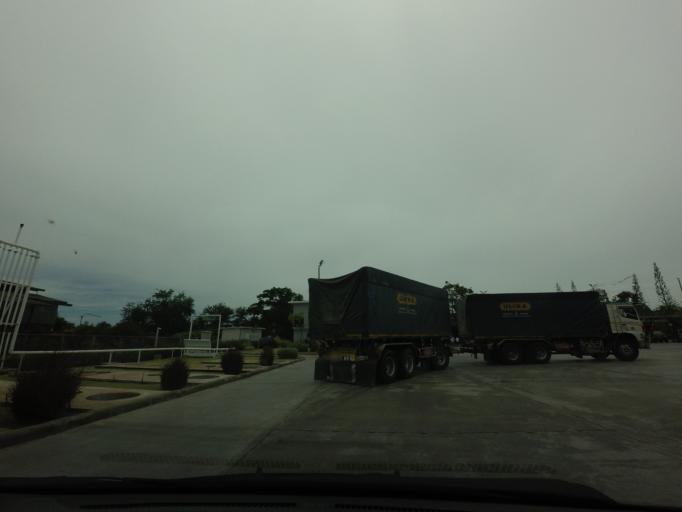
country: TH
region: Phetchaburi
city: Phetchaburi
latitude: 13.1184
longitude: 99.9074
